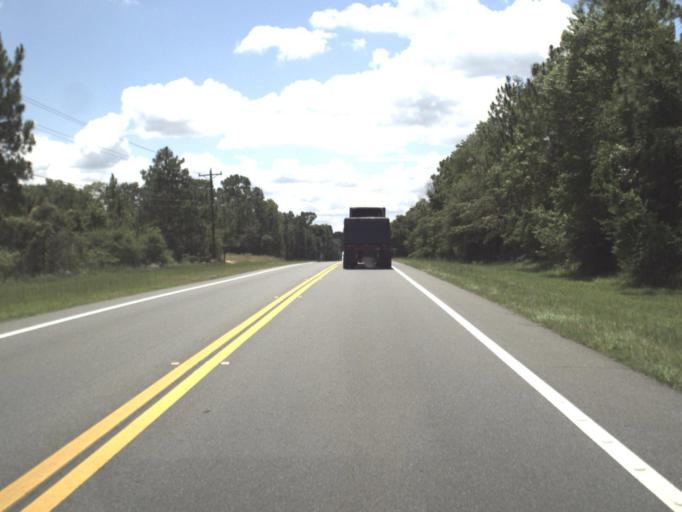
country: US
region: Florida
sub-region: Clay County
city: Keystone Heights
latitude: 29.7561
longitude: -81.9976
